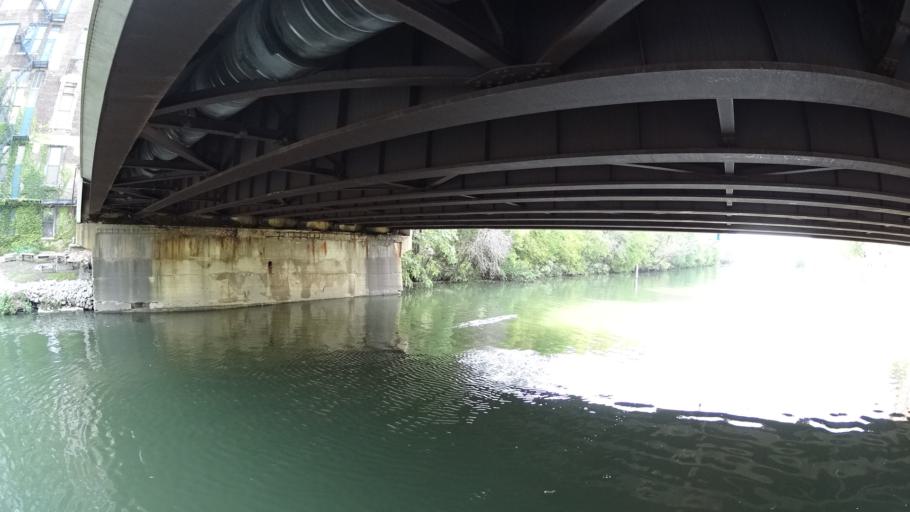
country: US
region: Illinois
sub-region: Cook County
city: Chicago
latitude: 41.8307
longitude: -87.6574
